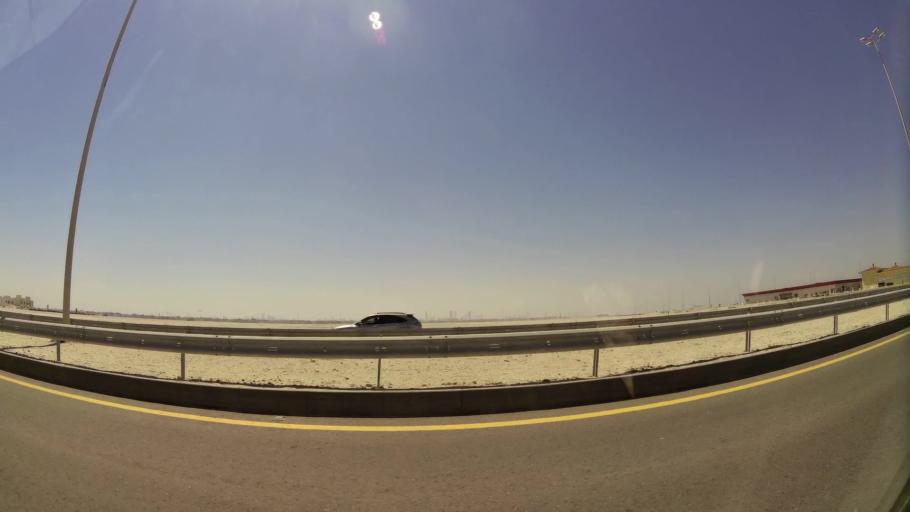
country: BH
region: Muharraq
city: Al Muharraq
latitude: 26.3050
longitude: 50.6306
